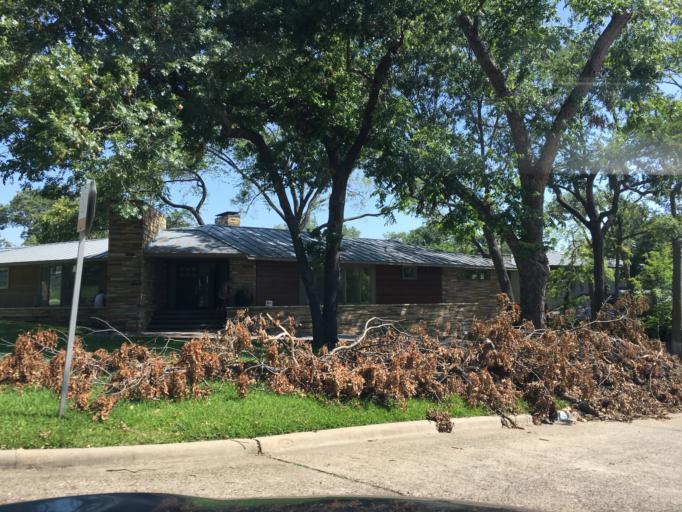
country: US
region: Texas
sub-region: Dallas County
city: University Park
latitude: 32.9077
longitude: -96.7778
